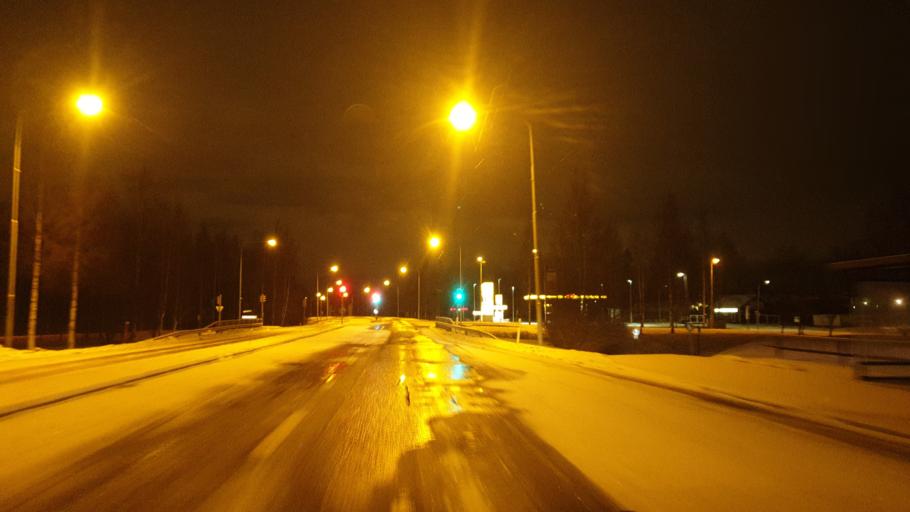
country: FI
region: Northern Ostrobothnia
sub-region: Oulu
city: Kempele
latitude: 64.9609
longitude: 25.5029
